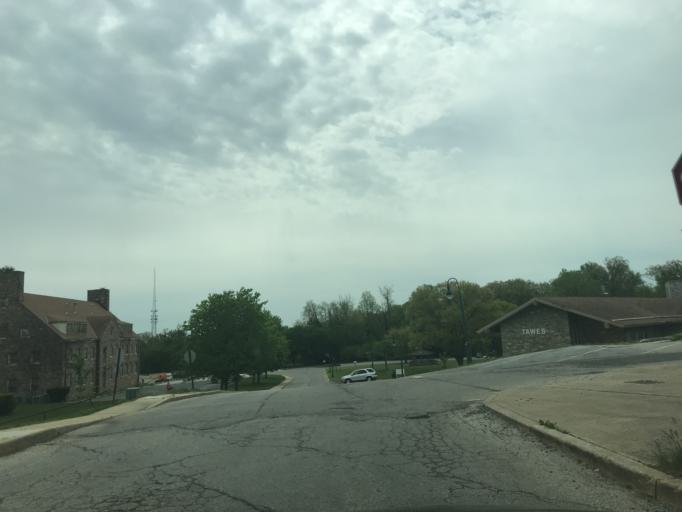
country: US
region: Maryland
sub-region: Baltimore County
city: Catonsville
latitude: 39.2646
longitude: -76.7210
